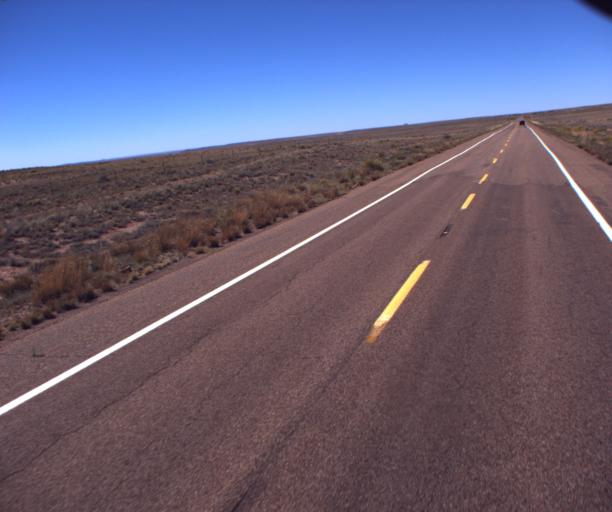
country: US
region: Arizona
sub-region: Navajo County
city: Holbrook
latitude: 34.7828
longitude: -109.8579
